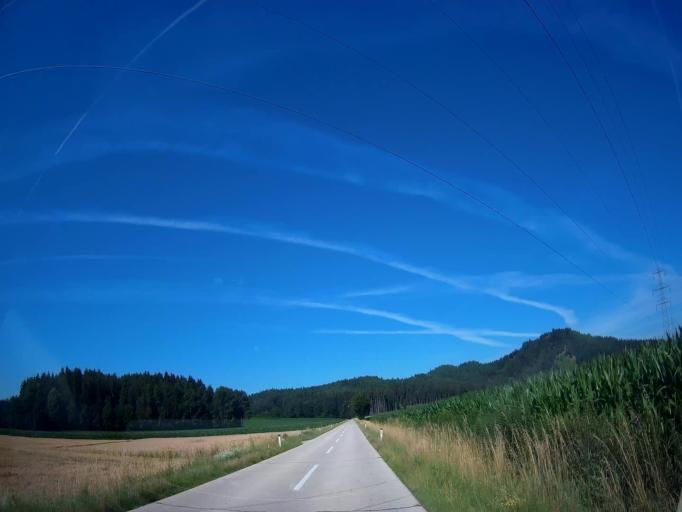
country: AT
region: Carinthia
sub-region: Politischer Bezirk Klagenfurt Land
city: Maria Saal
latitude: 46.7019
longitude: 14.4046
